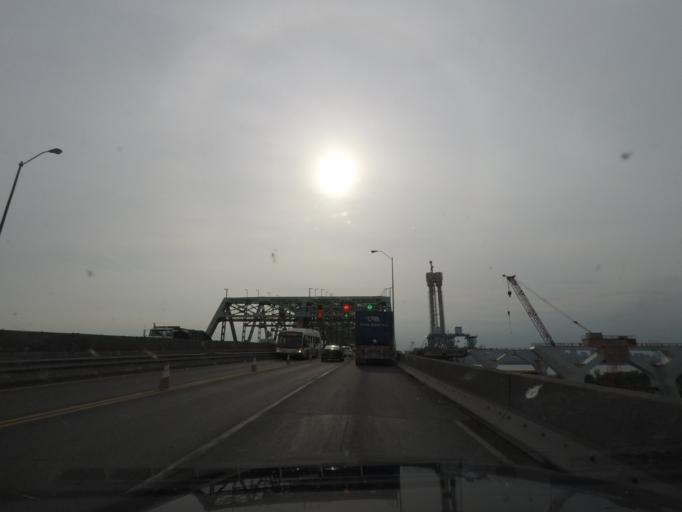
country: CA
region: Quebec
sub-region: Monteregie
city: Brossard
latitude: 45.4671
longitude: -73.5001
